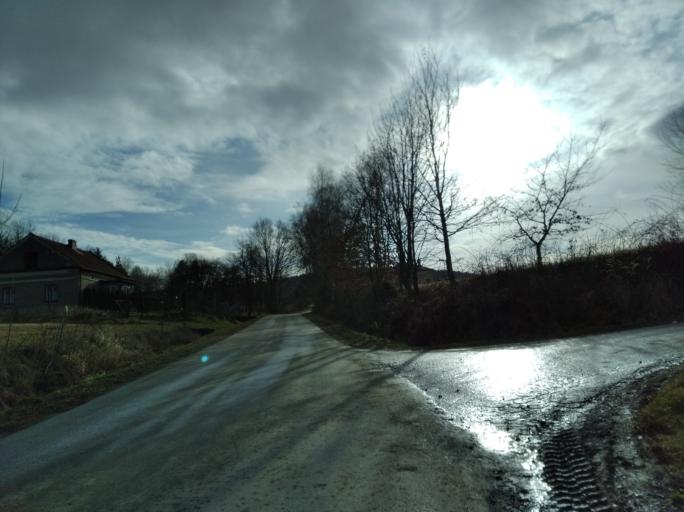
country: PL
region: Subcarpathian Voivodeship
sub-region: Powiat strzyzowski
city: Strzyzow
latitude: 49.8417
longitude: 21.7756
